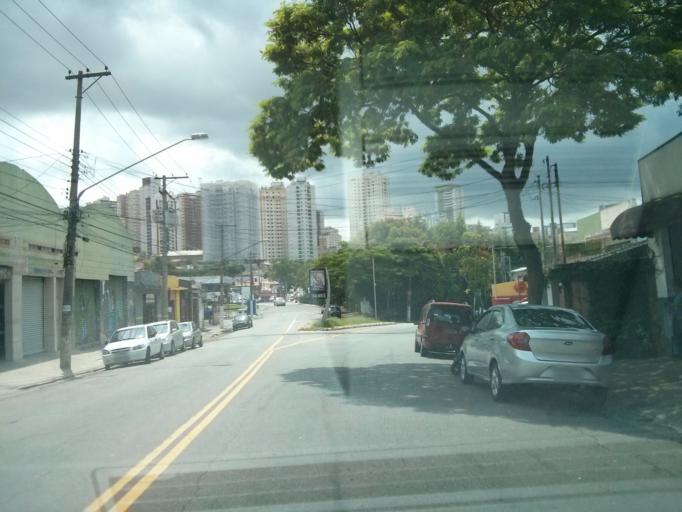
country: BR
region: Sao Paulo
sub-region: Sao Paulo
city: Sao Paulo
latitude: -23.6134
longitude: -46.6260
